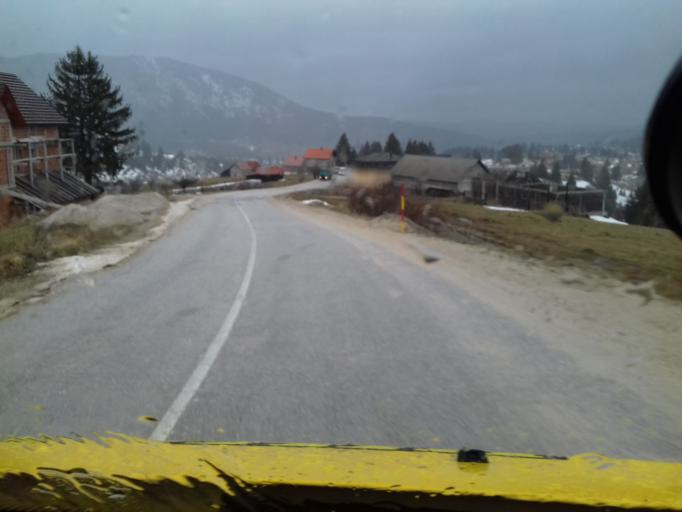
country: BA
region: Federation of Bosnia and Herzegovina
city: Turbe
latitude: 44.3143
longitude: 17.5664
